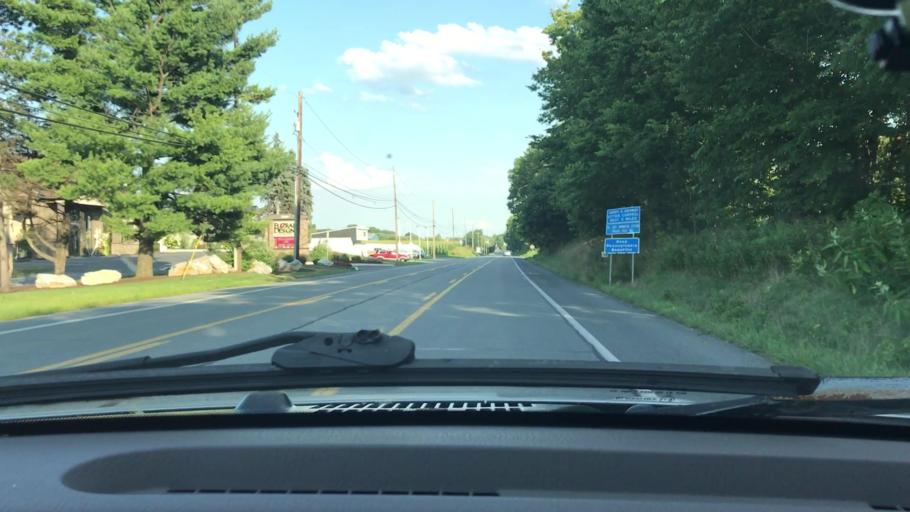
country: US
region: Pennsylvania
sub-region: Lancaster County
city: Rheems
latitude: 40.1234
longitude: -76.5447
